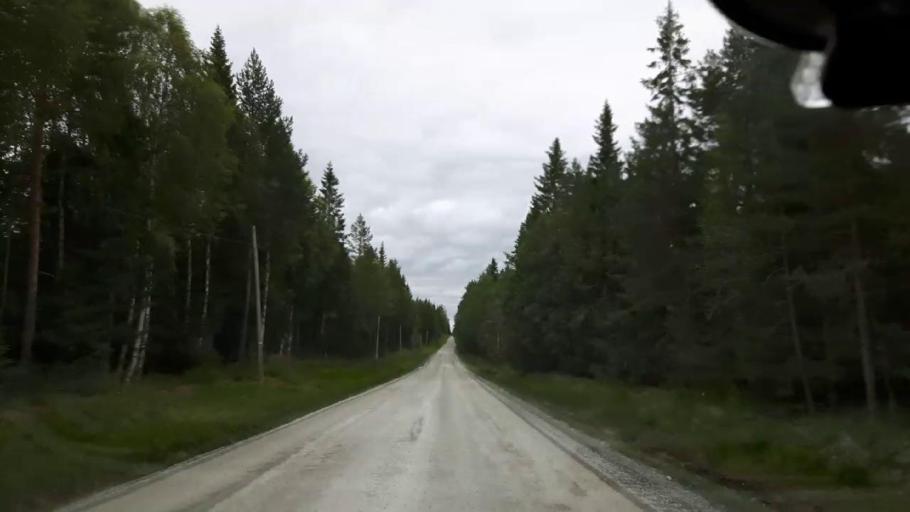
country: SE
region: Jaemtland
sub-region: OEstersunds Kommun
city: Brunflo
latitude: 63.0936
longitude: 15.1375
